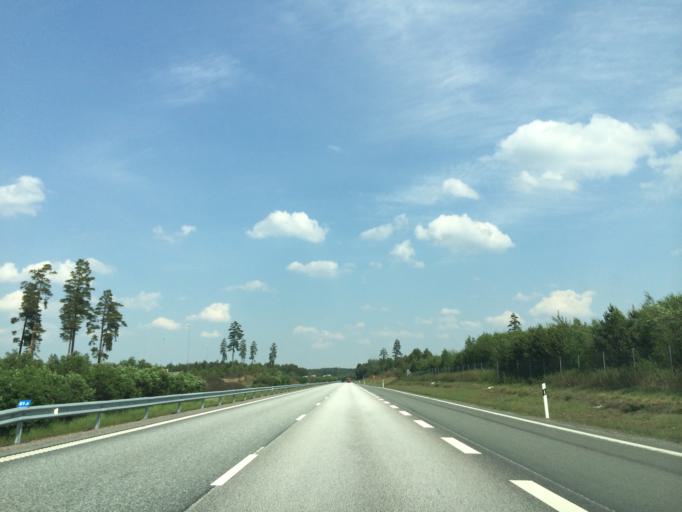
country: SE
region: Joenkoeping
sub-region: Vaggeryds Kommun
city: Vaggeryd
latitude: 57.5977
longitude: 14.1618
